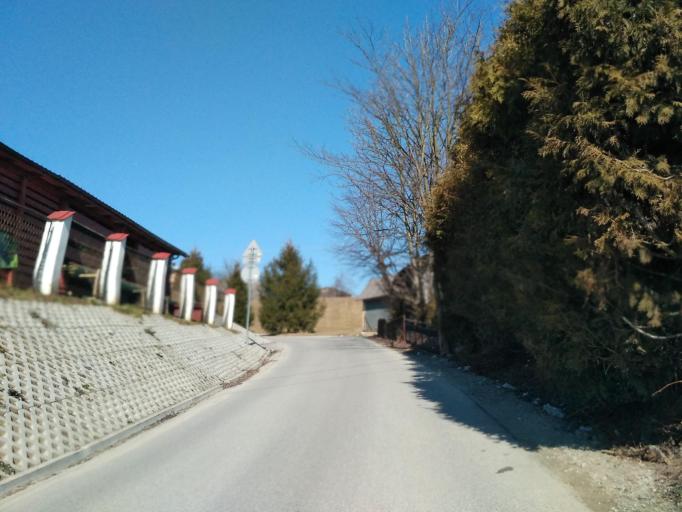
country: PL
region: Subcarpathian Voivodeship
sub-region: Powiat brzozowski
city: Jasienica Rosielna
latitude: 49.7527
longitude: 21.9435
